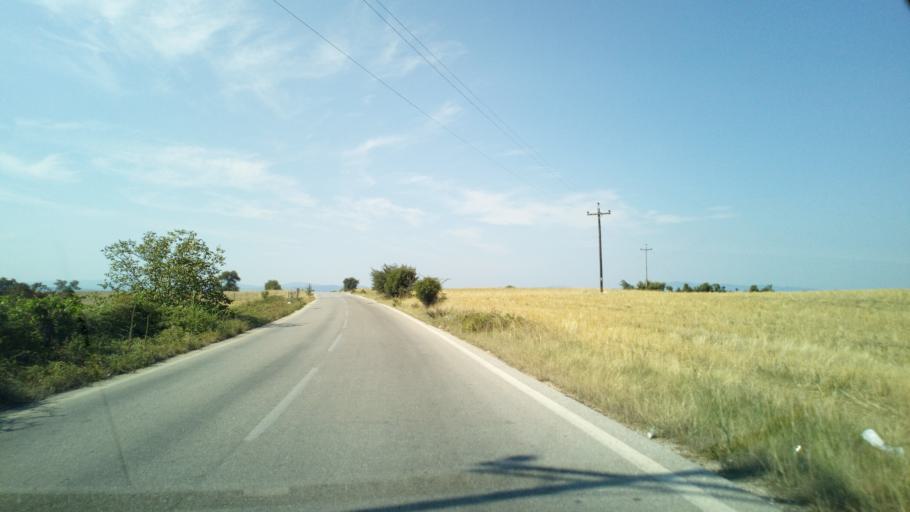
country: GR
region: Central Macedonia
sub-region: Nomos Thessalonikis
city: Nea Apollonia
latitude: 40.5081
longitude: 23.4747
